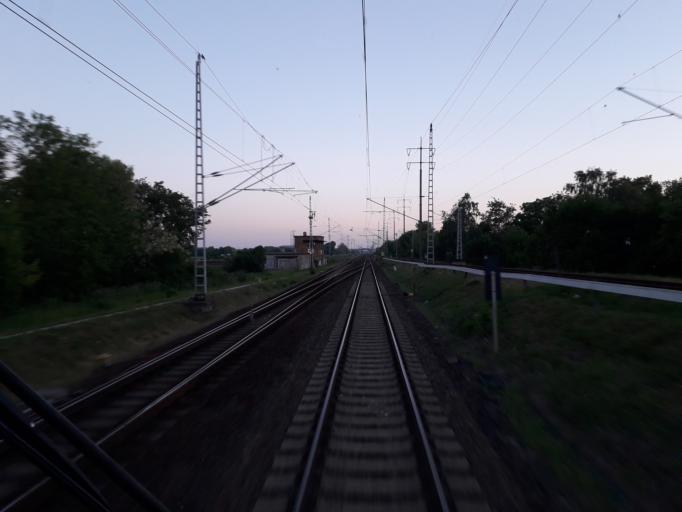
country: DE
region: Berlin
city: Blankenburg
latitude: 52.6109
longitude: 13.4545
